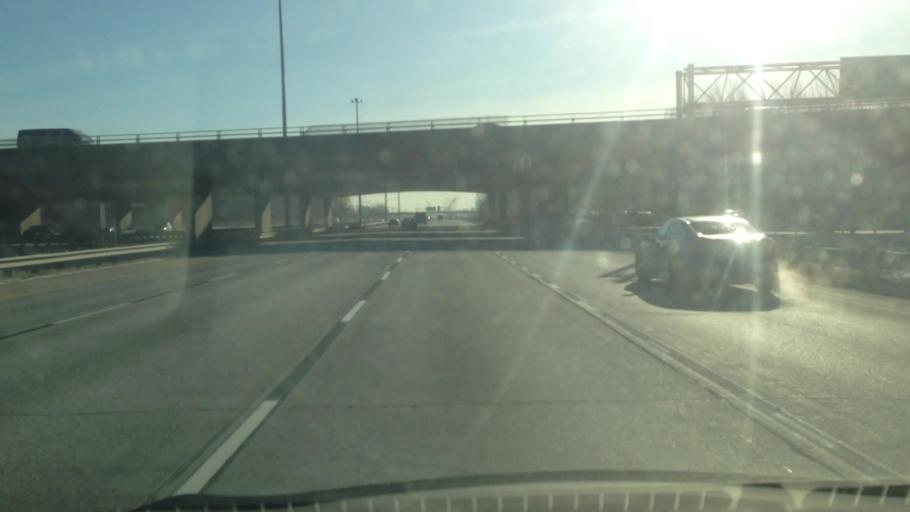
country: CA
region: Quebec
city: Dollard-Des Ormeaux
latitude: 45.5553
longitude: -73.8102
